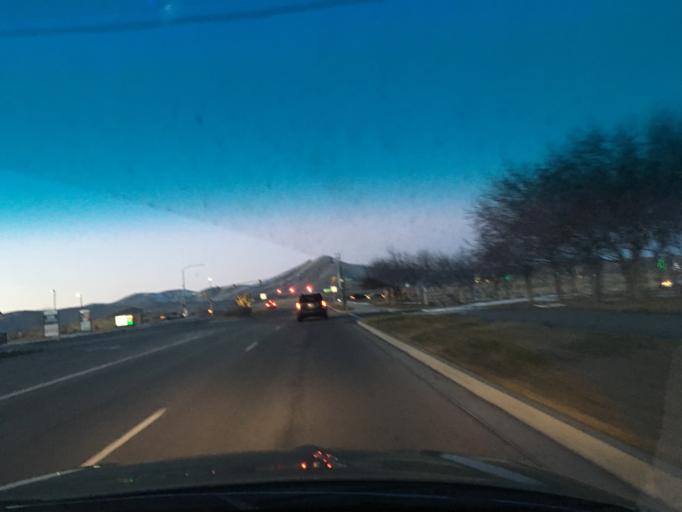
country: US
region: Utah
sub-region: Utah County
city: Eagle Mountain
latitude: 40.3792
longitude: -111.9738
